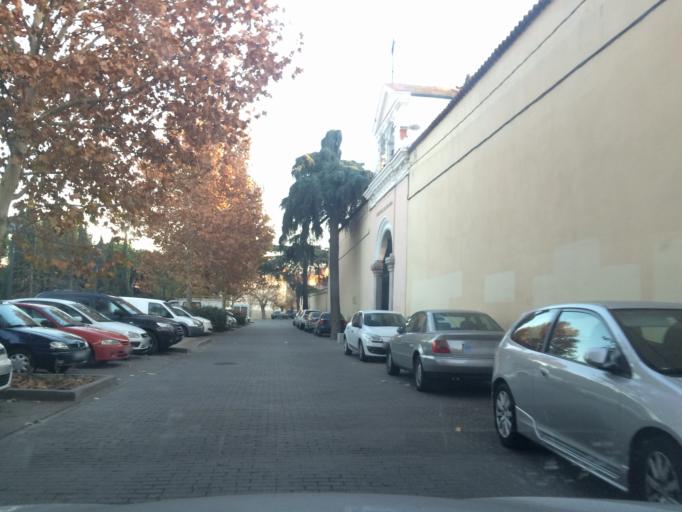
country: ES
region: Madrid
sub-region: Provincia de Madrid
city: Carabanchel
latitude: 40.3983
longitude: -3.7220
